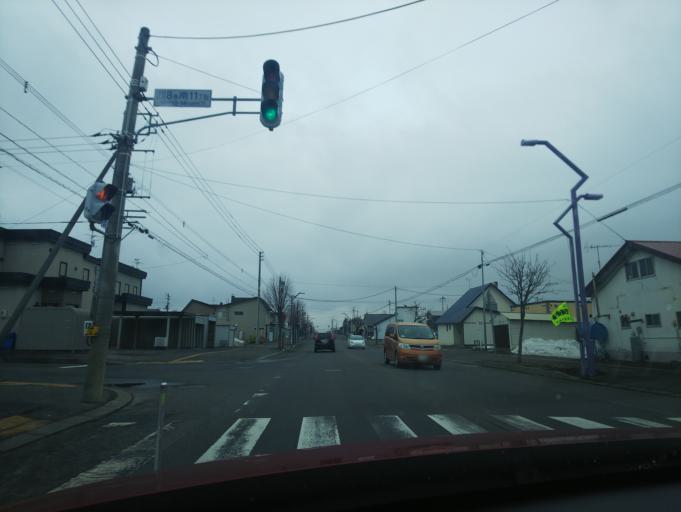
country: JP
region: Hokkaido
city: Nayoro
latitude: 44.3438
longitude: 142.4503
